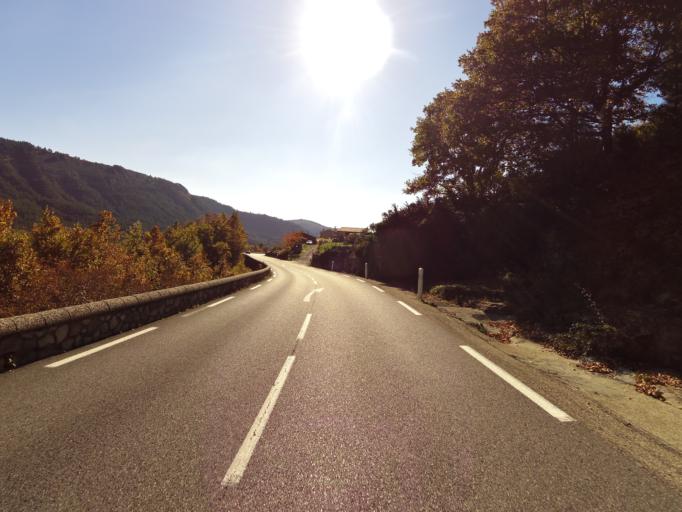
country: FR
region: Rhone-Alpes
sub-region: Departement de l'Ardeche
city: Vesseaux
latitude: 44.6766
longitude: 4.4605
